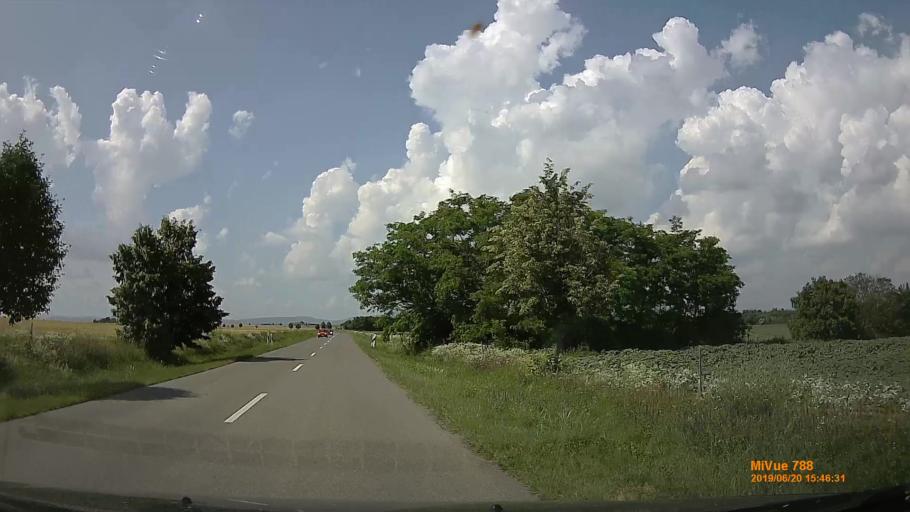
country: HU
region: Baranya
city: Kozarmisleny
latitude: 45.9976
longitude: 18.2432
